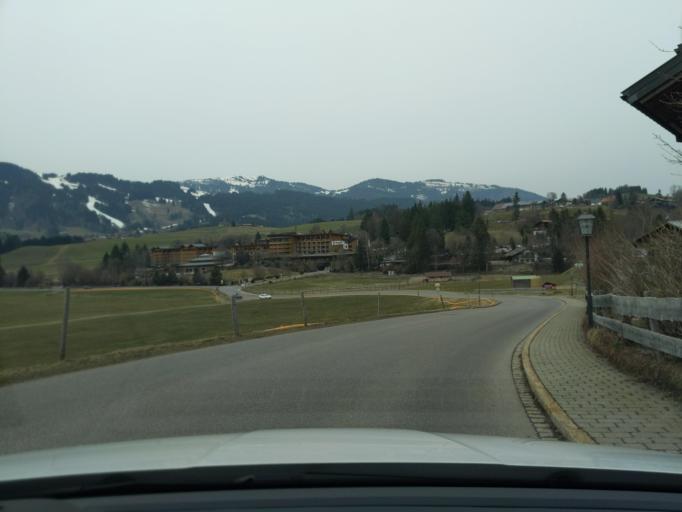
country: DE
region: Bavaria
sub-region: Swabia
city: Ofterschwang
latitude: 47.4879
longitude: 10.2606
